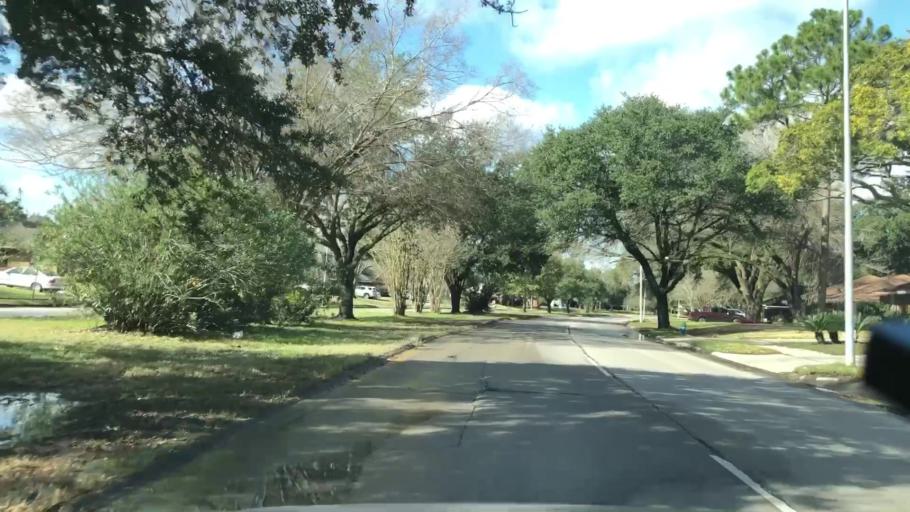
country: US
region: Texas
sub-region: Harris County
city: Bellaire
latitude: 29.6644
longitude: -95.4658
